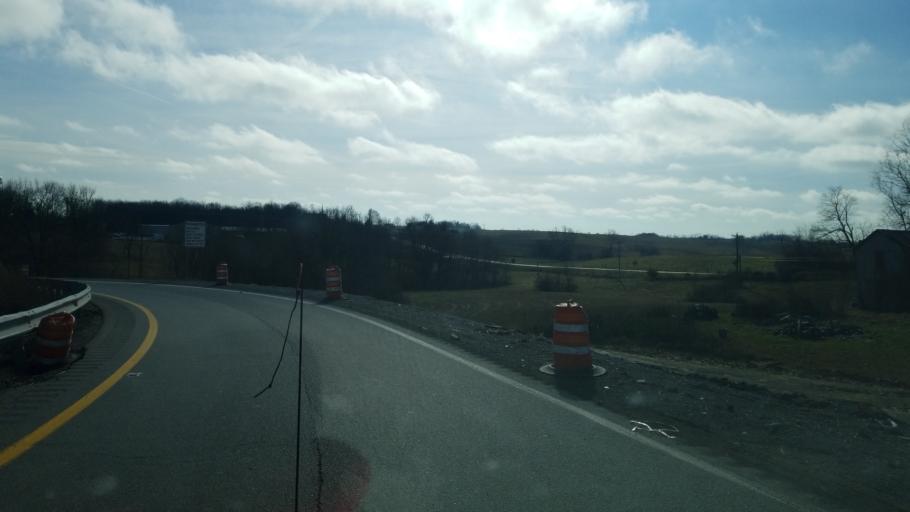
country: US
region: Kentucky
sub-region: Madison County
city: Richmond
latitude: 37.8432
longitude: -84.3282
